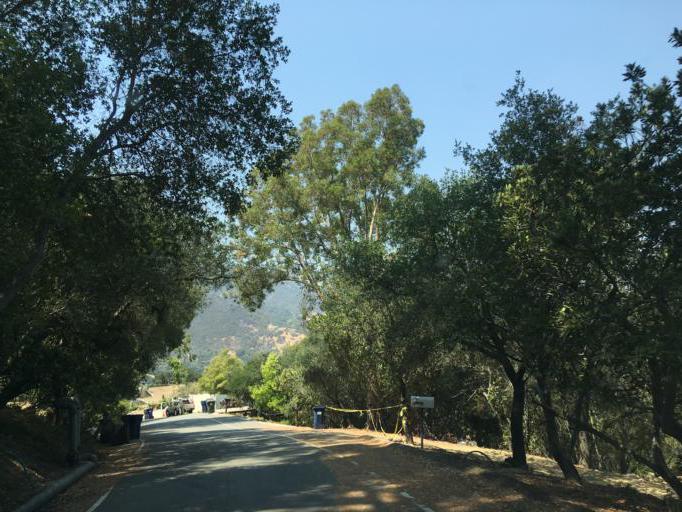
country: US
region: California
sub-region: Los Angeles County
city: Topanga
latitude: 34.0894
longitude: -118.5979
